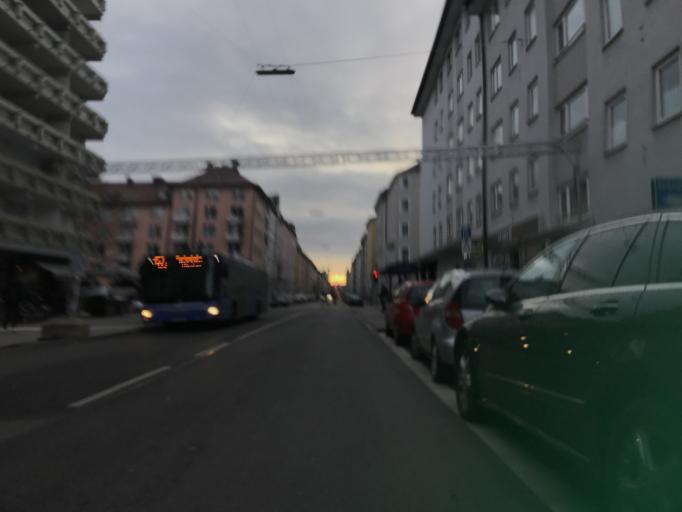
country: DE
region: Bavaria
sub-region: Upper Bavaria
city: Munich
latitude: 48.1527
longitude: 11.5675
